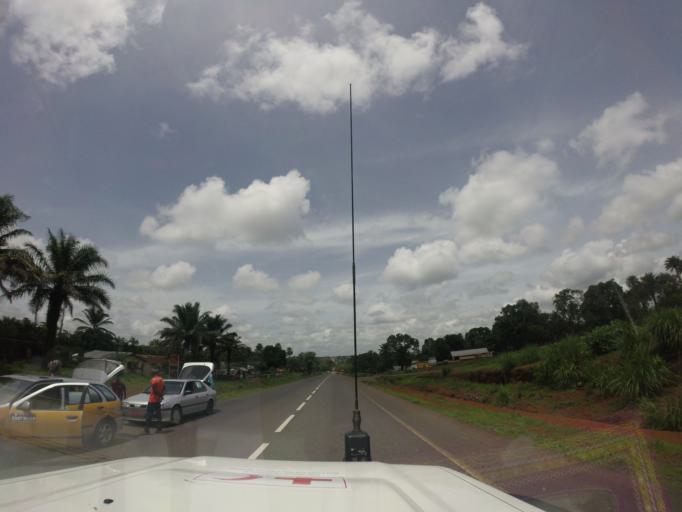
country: SL
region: Northern Province
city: Kambia
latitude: 9.1259
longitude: -12.9359
